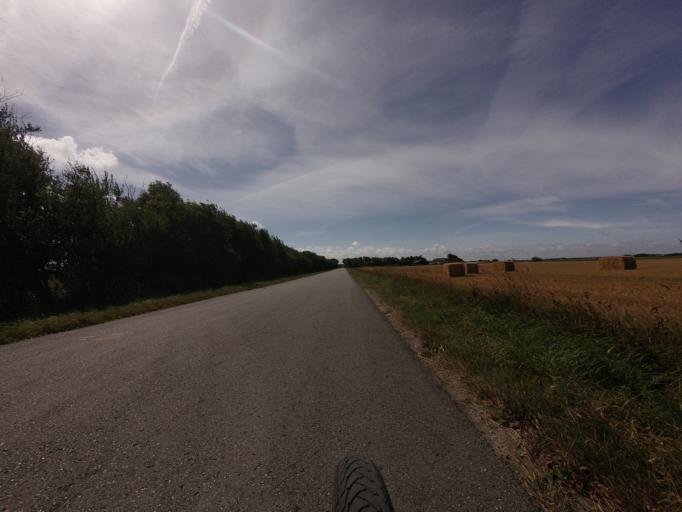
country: DK
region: North Denmark
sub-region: Bronderslev Kommune
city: Bronderslev
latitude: 57.3218
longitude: 9.8158
